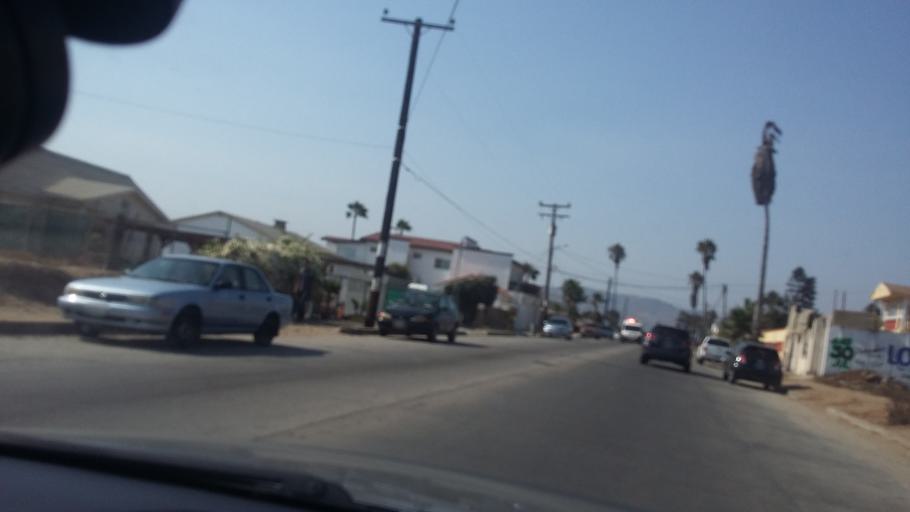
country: MX
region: Baja California
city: Ensenada
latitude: 31.8318
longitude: -116.6091
